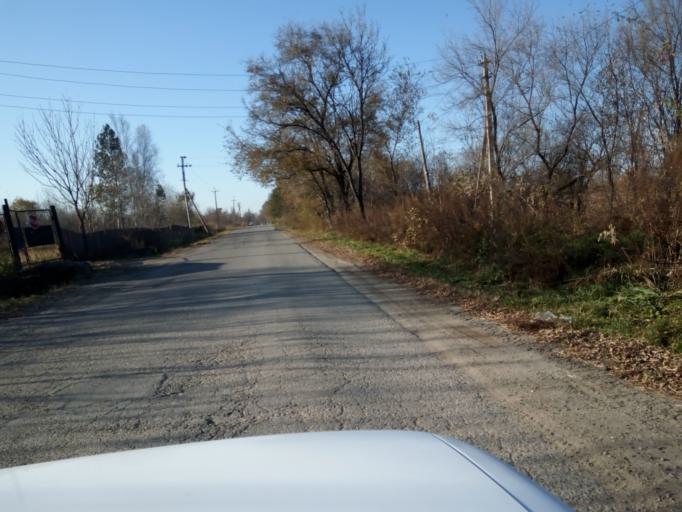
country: RU
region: Primorskiy
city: Lazo
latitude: 45.8800
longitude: 133.6467
